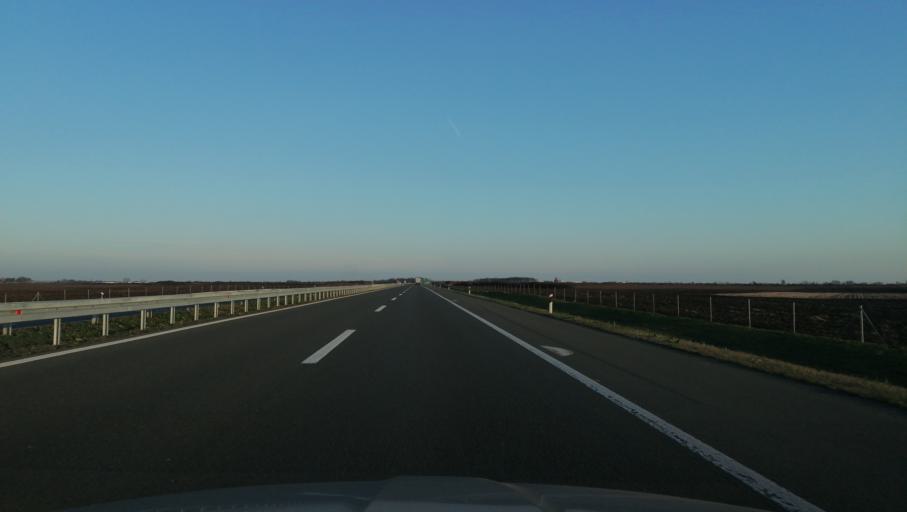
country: RS
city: Sasinci
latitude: 44.9685
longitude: 19.7788
